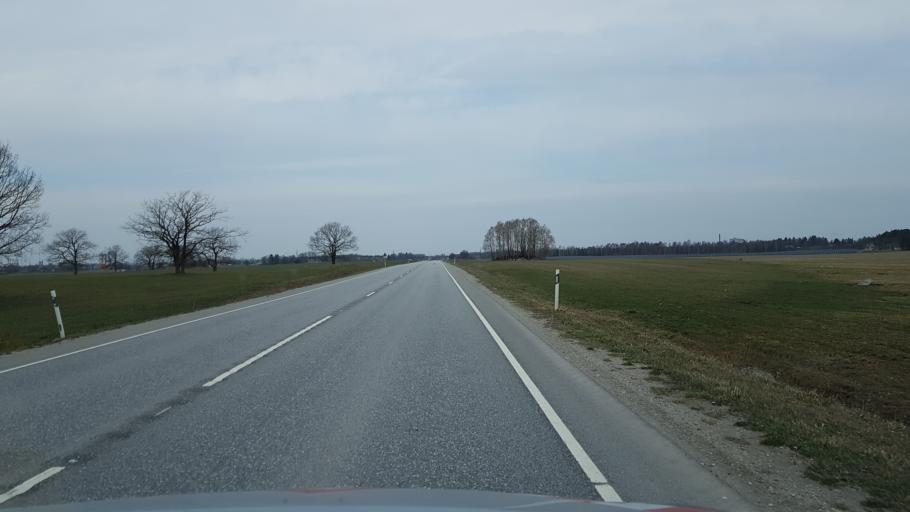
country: EE
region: Laeaene-Virumaa
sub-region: Someru vald
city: Someru
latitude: 59.3470
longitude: 26.4062
